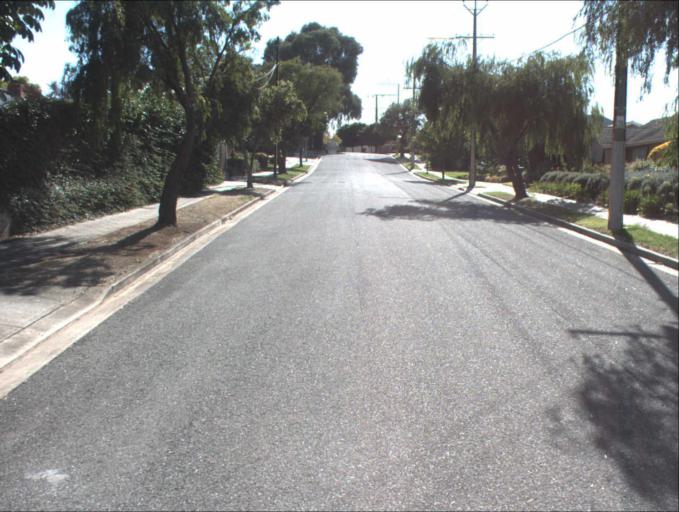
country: AU
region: South Australia
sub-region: Port Adelaide Enfield
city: Gilles Plains
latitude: -34.8644
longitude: 138.6562
